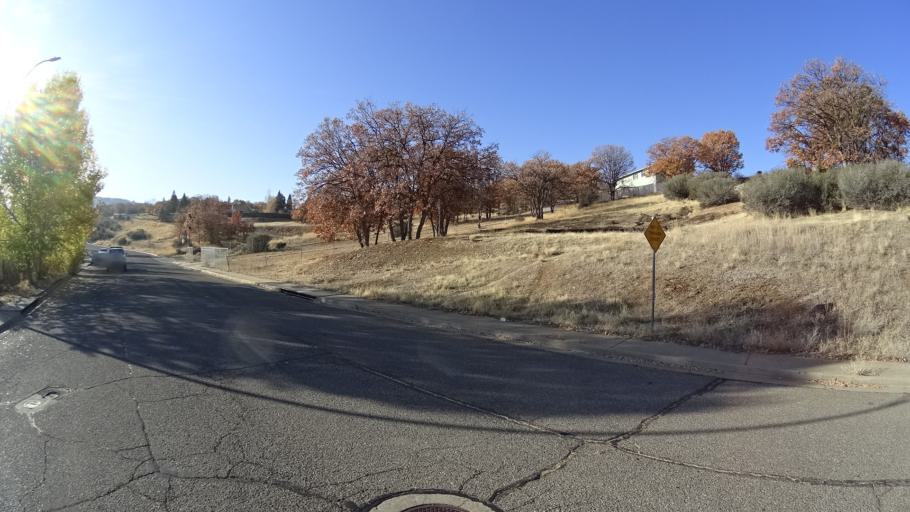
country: US
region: California
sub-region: Siskiyou County
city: Yreka
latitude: 41.7093
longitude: -122.6238
